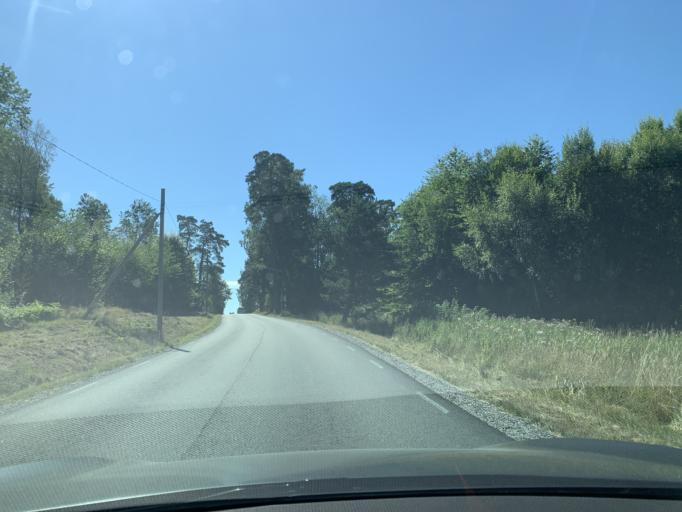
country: SE
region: Stockholm
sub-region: Botkyrka Kommun
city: Eriksberg
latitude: 59.2447
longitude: 17.7872
